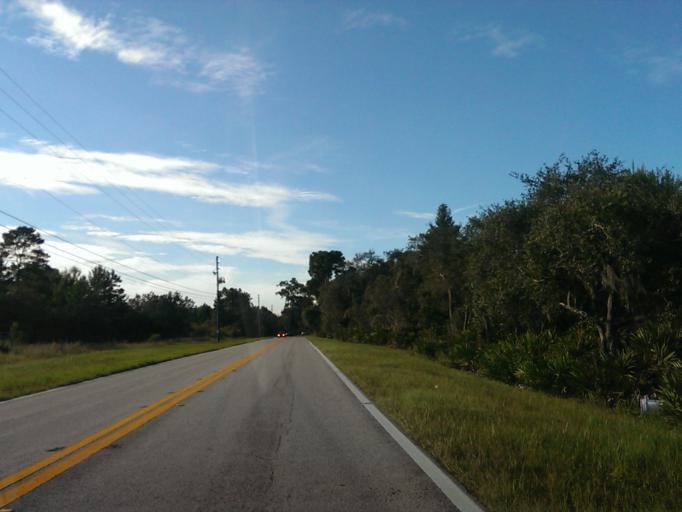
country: US
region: Florida
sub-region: Polk County
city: Citrus Ridge
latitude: 28.3529
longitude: -81.6465
